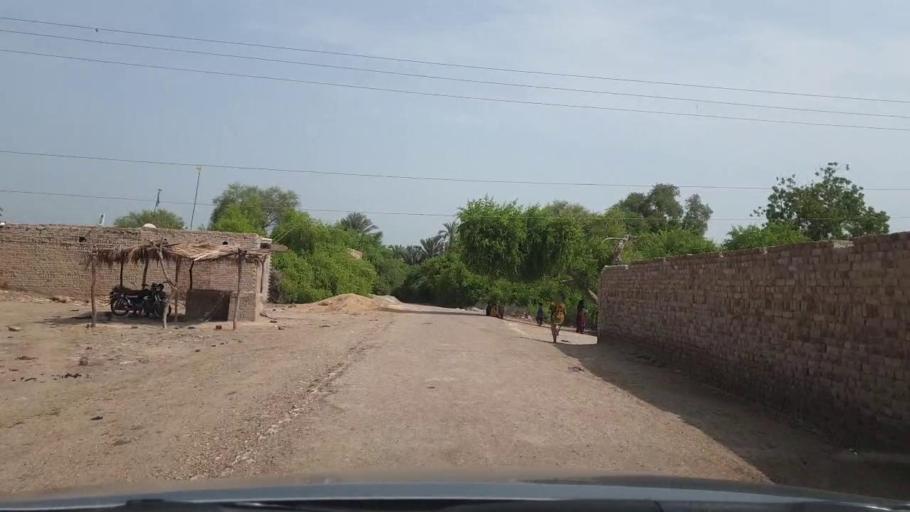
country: PK
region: Sindh
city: Rohri
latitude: 27.6468
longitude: 69.0235
